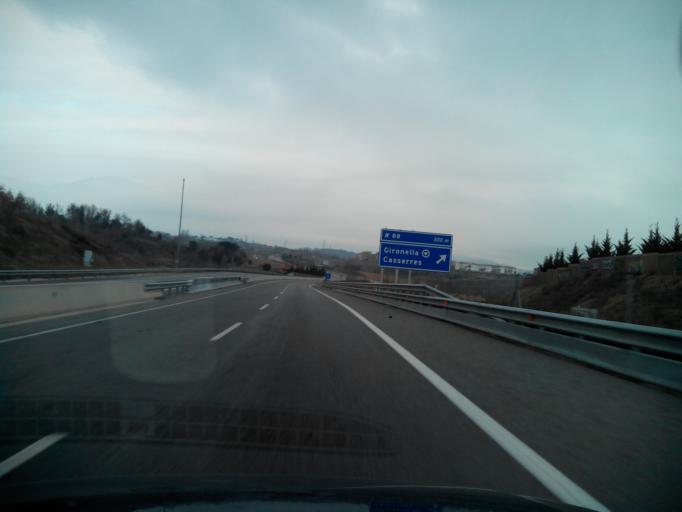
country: ES
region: Catalonia
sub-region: Provincia de Barcelona
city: Gironella
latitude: 42.0235
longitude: 1.8777
